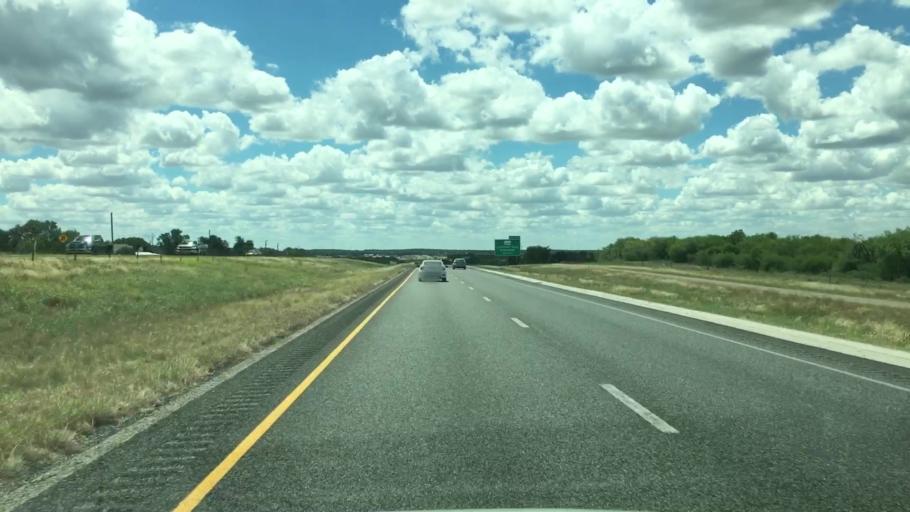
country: US
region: Texas
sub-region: Bexar County
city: Elmendorf
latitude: 29.2439
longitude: -98.3981
